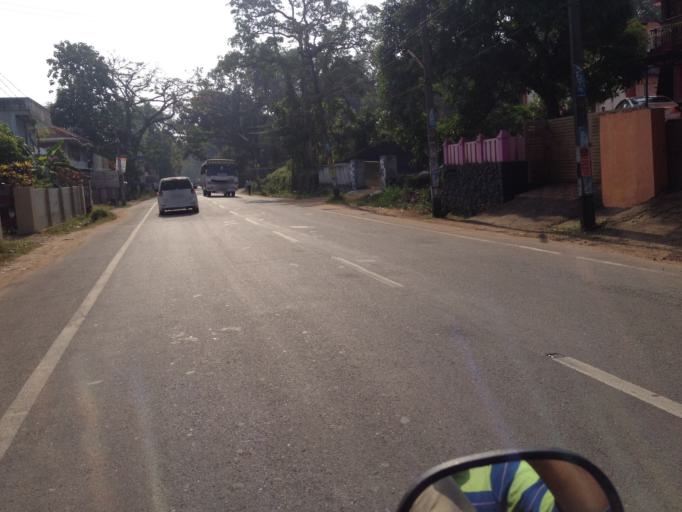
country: IN
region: Kerala
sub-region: Pattanamtitta
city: Adur
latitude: 9.1522
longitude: 76.7441
